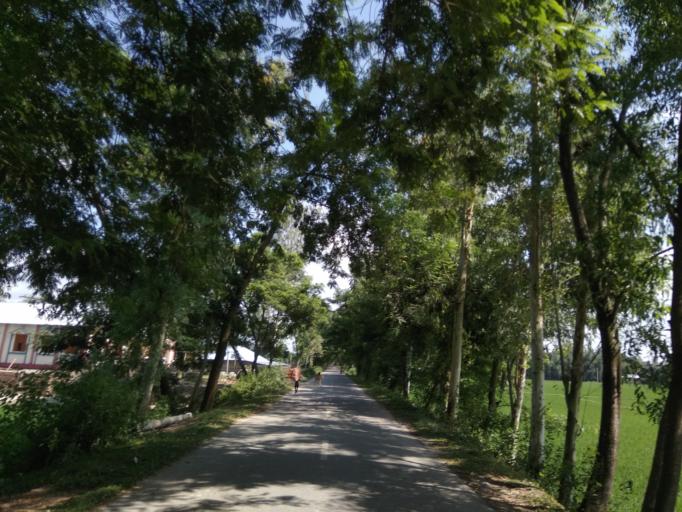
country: IN
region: West Bengal
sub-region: Koch Bihar
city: Haldibari
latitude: 26.1970
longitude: 88.6886
